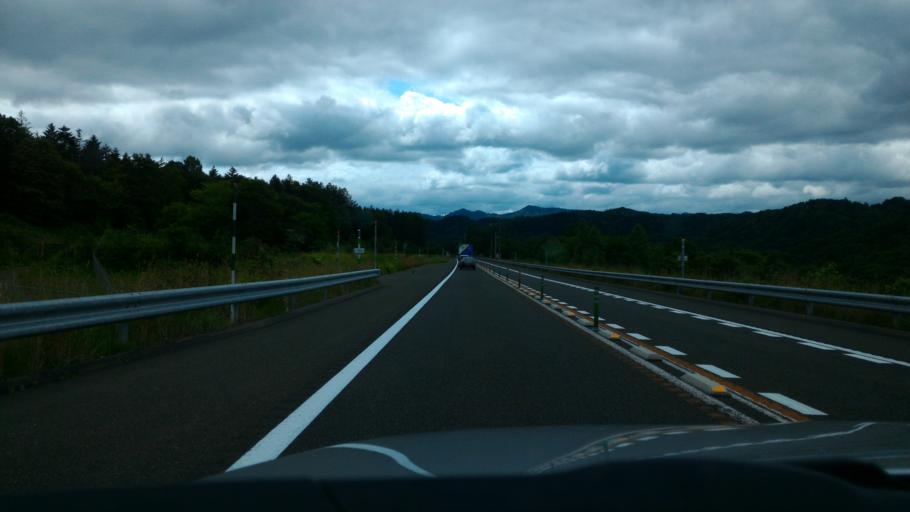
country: JP
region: Hokkaido
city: Shimo-furano
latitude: 42.9455
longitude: 142.2261
